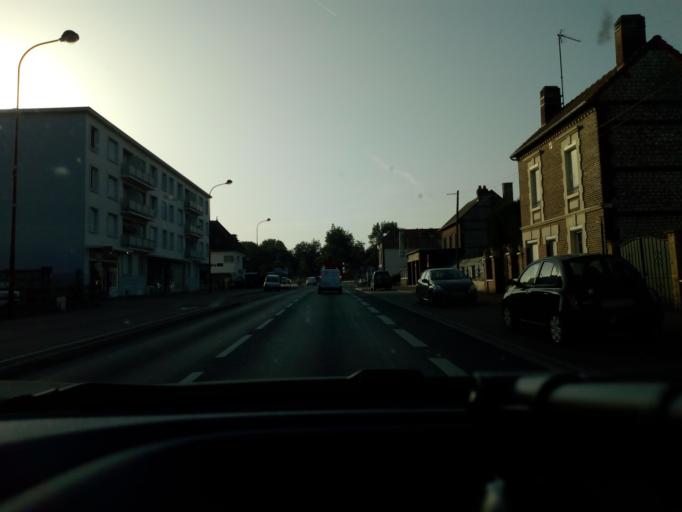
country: FR
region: Haute-Normandie
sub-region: Departement de la Seine-Maritime
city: Le Petit-Quevilly
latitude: 49.4127
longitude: 1.0705
